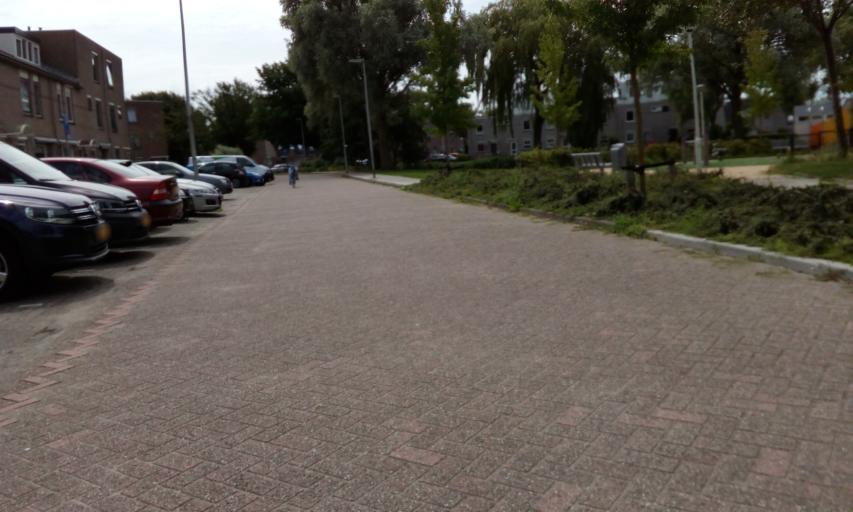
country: NL
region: South Holland
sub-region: Gemeente Zoetermeer
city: Zoetermeer
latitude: 52.0428
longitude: 4.4915
